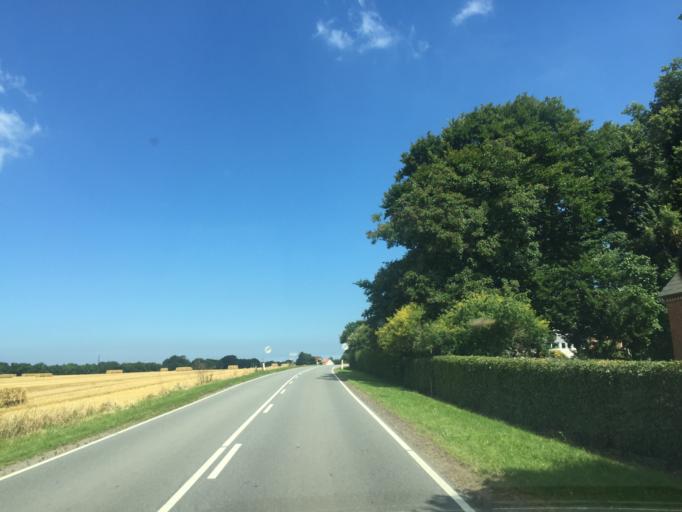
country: DK
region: South Denmark
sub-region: Nordfyns Kommune
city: Otterup
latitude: 55.5614
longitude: 10.3738
